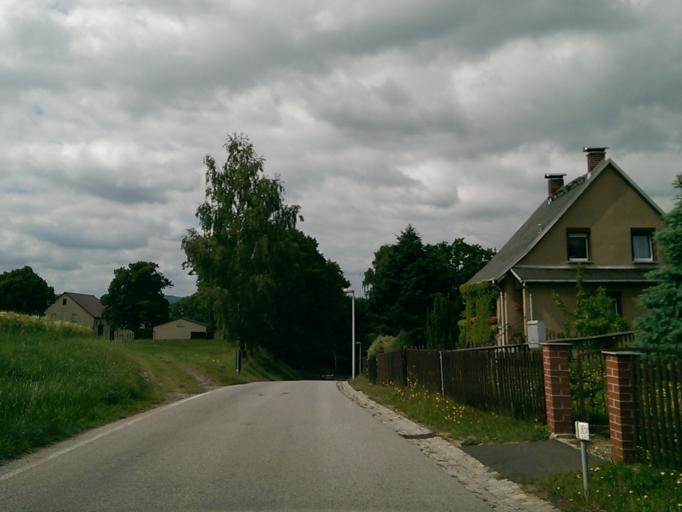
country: DE
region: Saxony
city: Mittelherwigsdorf
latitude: 50.9383
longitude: 14.7700
